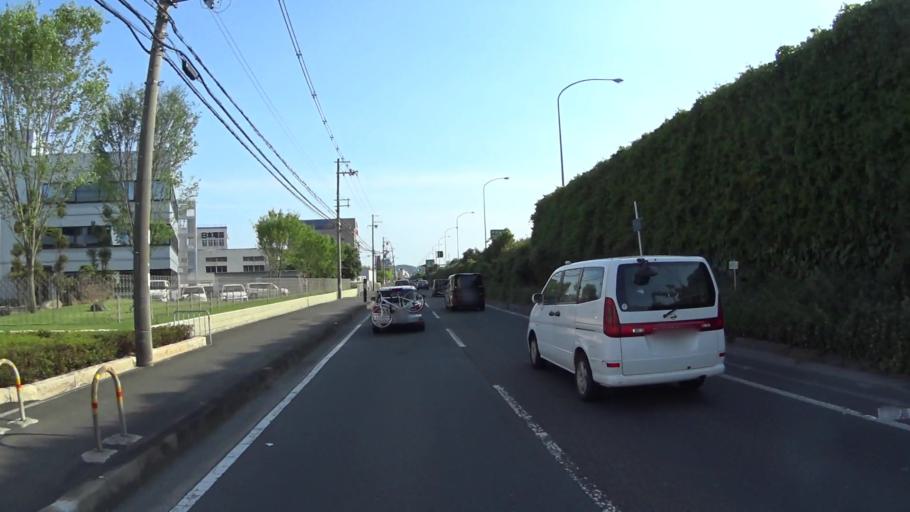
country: JP
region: Kyoto
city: Muko
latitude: 34.9210
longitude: 135.7145
